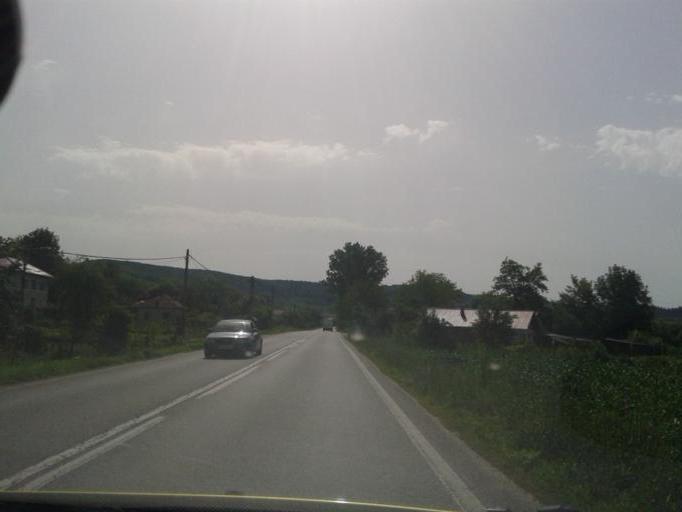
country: RO
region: Valcea
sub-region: Comuna Mihaesti
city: Mihaesti
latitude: 45.0640
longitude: 24.2347
